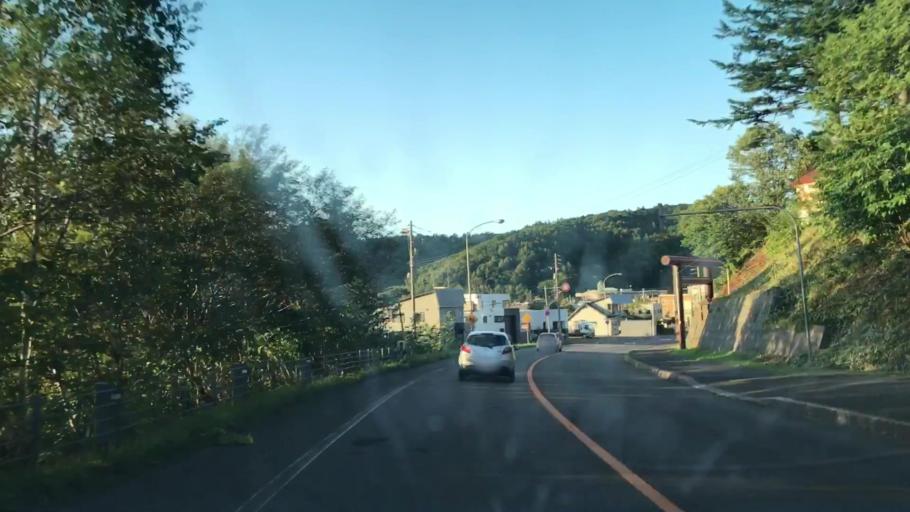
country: JP
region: Hokkaido
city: Niseko Town
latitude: 42.7923
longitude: 140.9349
